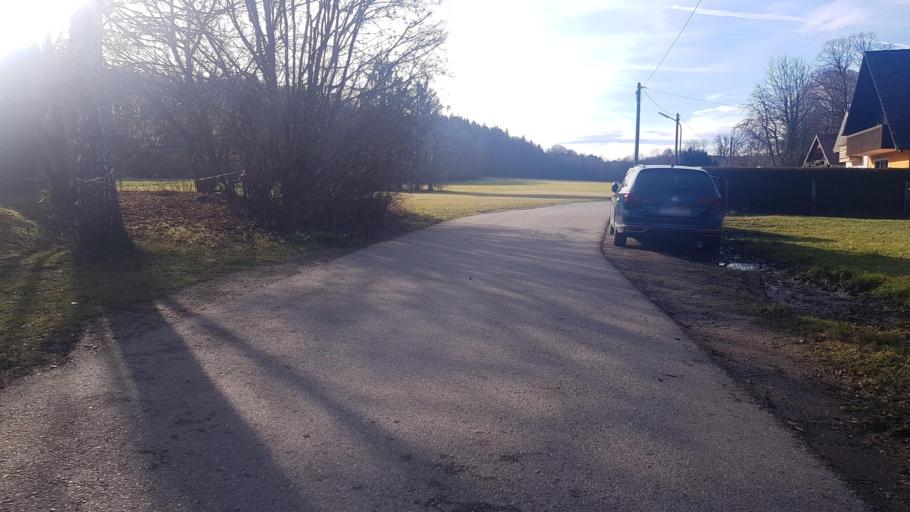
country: DE
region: Bavaria
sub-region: Upper Bavaria
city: Gauting
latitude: 48.0565
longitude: 11.3788
